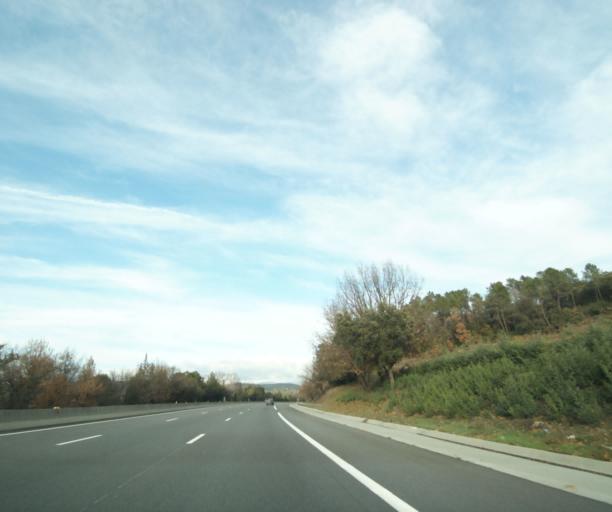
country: FR
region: Provence-Alpes-Cote d'Azur
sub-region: Departement du Var
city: Les Arcs
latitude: 43.4340
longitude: 6.4670
